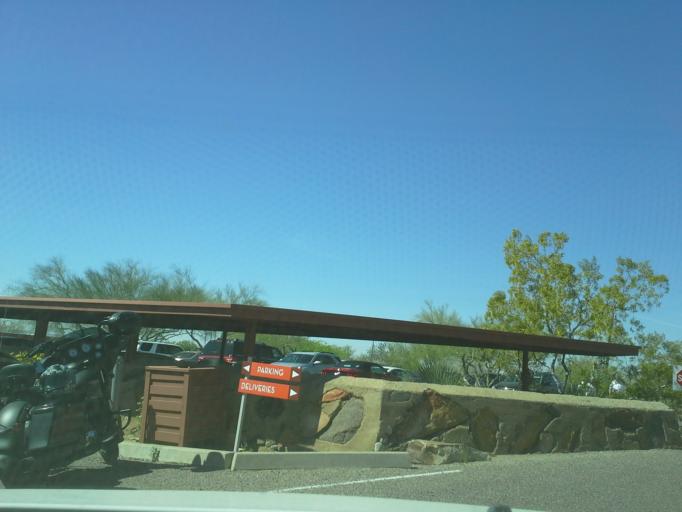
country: US
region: Arizona
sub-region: Maricopa County
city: Scottsdale
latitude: 33.6070
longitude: -111.8463
